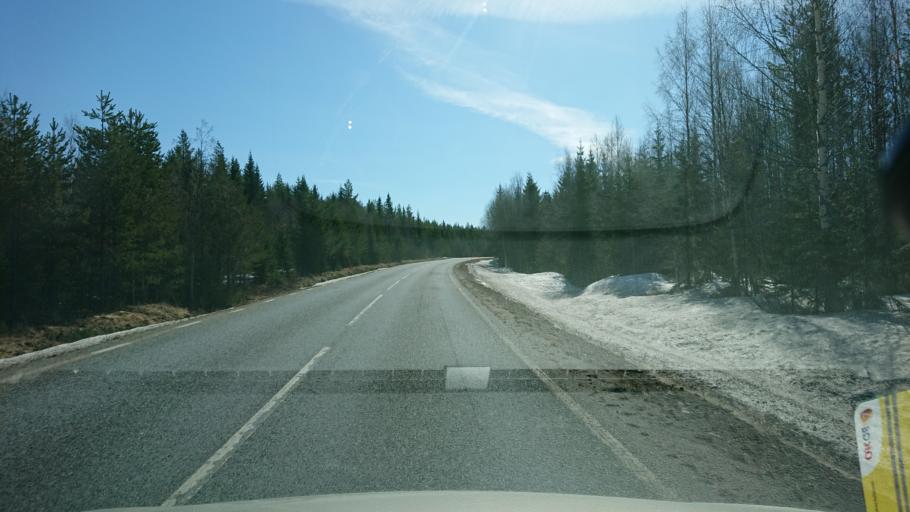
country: SE
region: Vaesterbotten
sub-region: Dorotea Kommun
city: Dorotea
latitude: 63.9945
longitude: 16.3129
